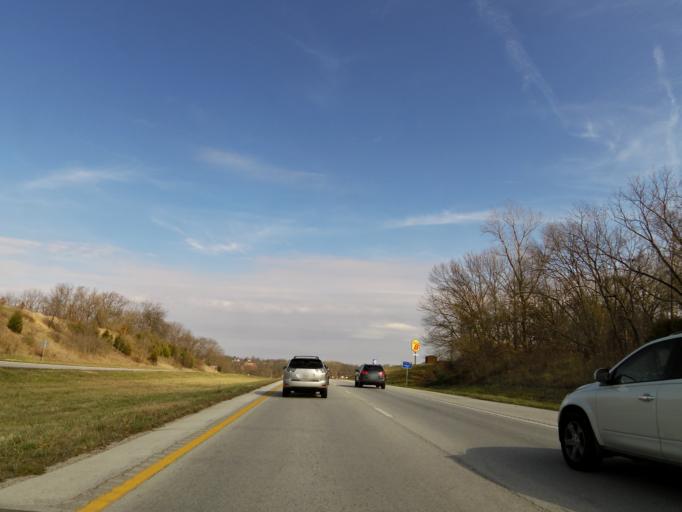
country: US
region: Missouri
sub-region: Marion County
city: Hannibal
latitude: 39.6982
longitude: -91.3912
